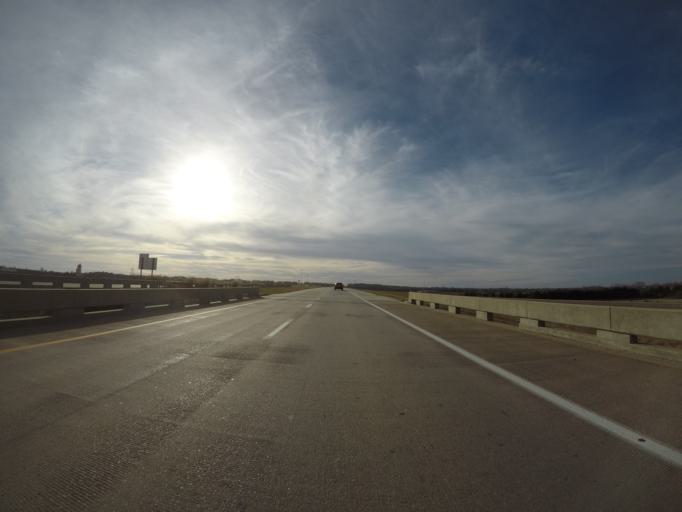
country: US
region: Kansas
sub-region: Franklin County
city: Ottawa
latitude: 38.5757
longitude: -95.2679
